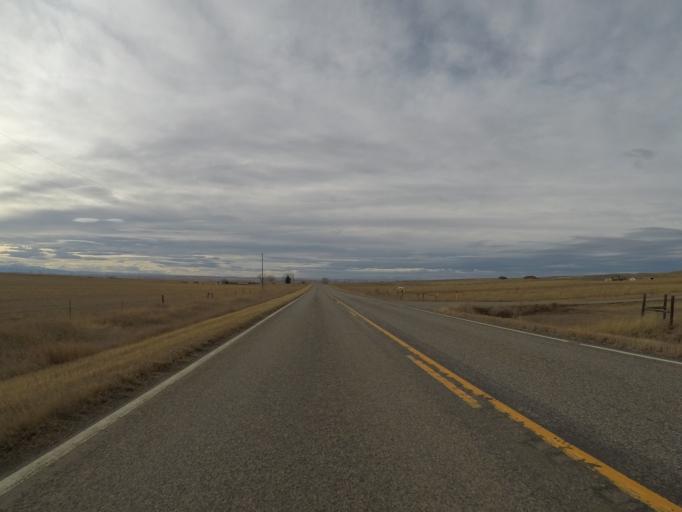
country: US
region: Montana
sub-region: Yellowstone County
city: Laurel
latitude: 45.8566
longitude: -108.8329
